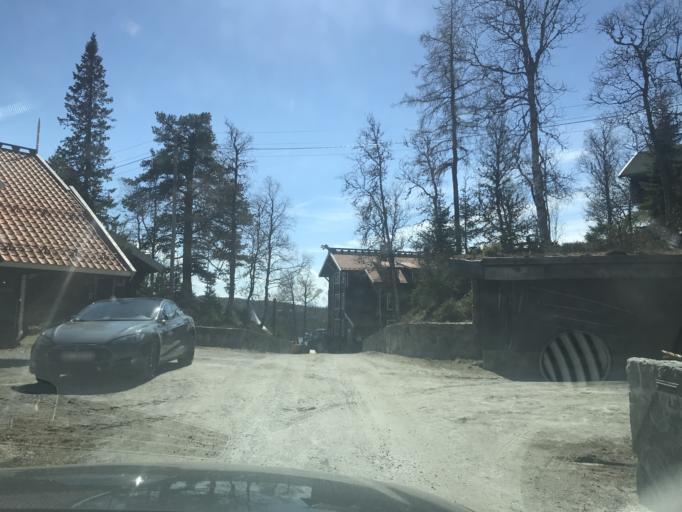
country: NO
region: Telemark
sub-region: Tinn
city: Rjukan
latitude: 59.7946
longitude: 8.7482
